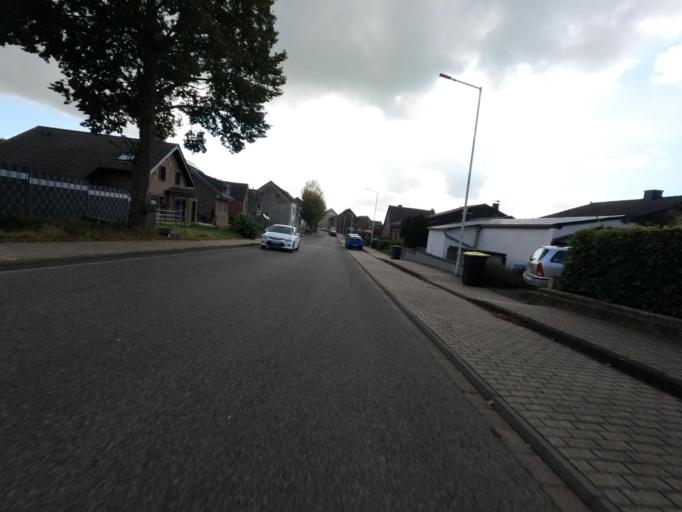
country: DE
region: North Rhine-Westphalia
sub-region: Regierungsbezirk Koln
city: Linnich
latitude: 51.0053
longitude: 6.2808
